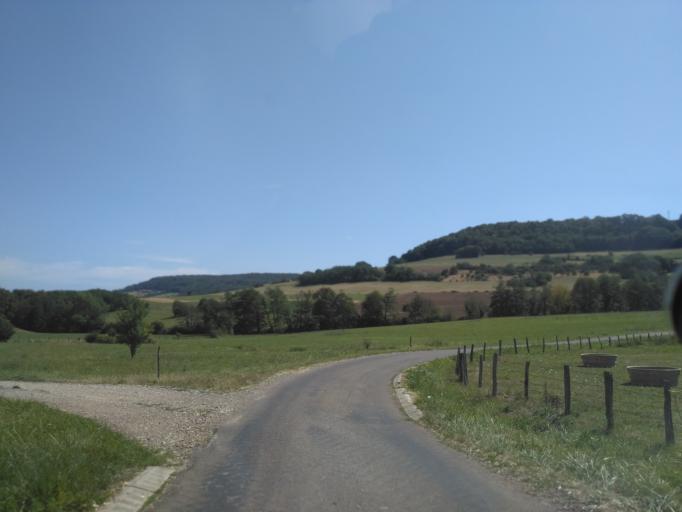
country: FR
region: Franche-Comte
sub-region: Departement de la Haute-Saone
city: Villersexel
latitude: 47.5082
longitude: 6.5193
